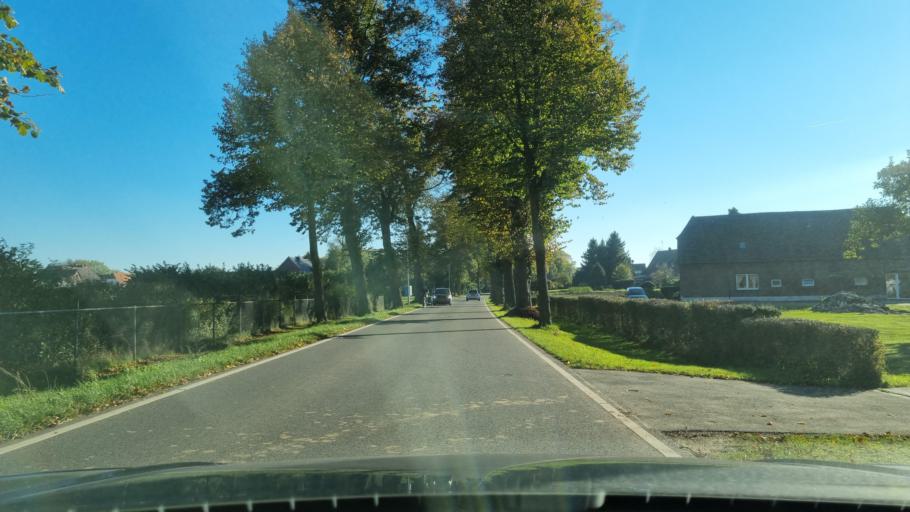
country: DE
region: North Rhine-Westphalia
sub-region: Regierungsbezirk Dusseldorf
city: Kranenburg
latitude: 51.7789
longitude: 6.0204
